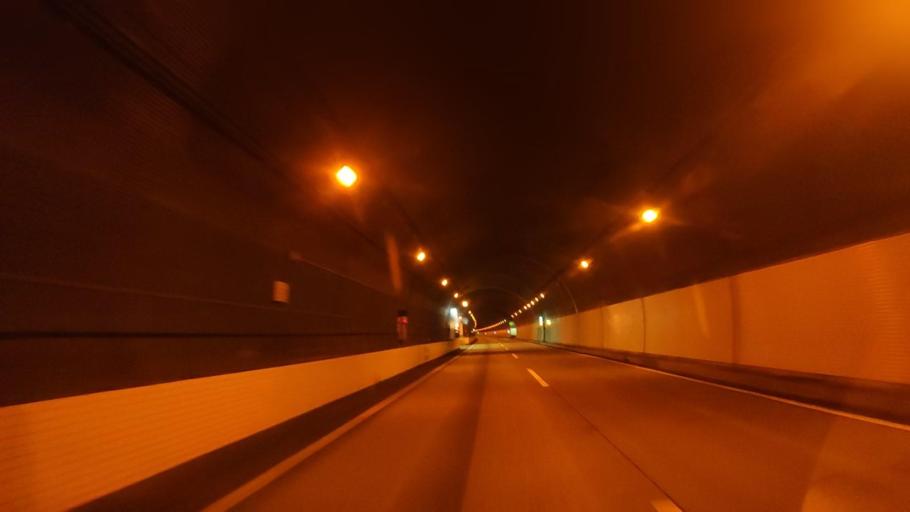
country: JP
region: Toyama
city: Nyuzen
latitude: 36.9788
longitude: 137.6602
